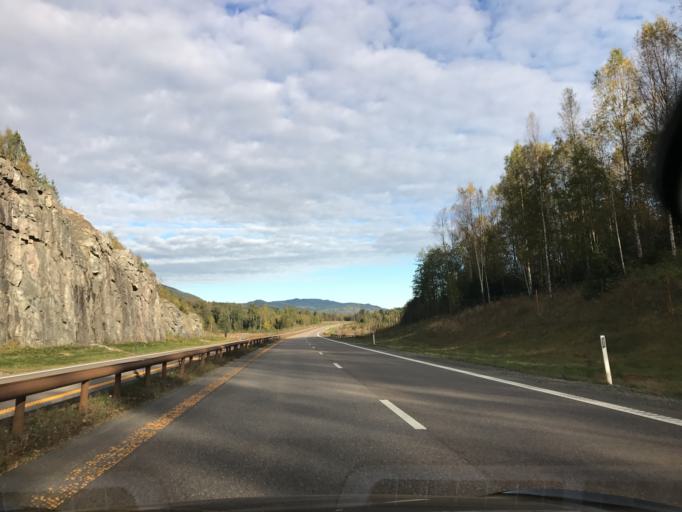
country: NO
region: Akershus
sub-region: Eidsvoll
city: Eidsvoll
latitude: 60.3559
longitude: 11.2067
